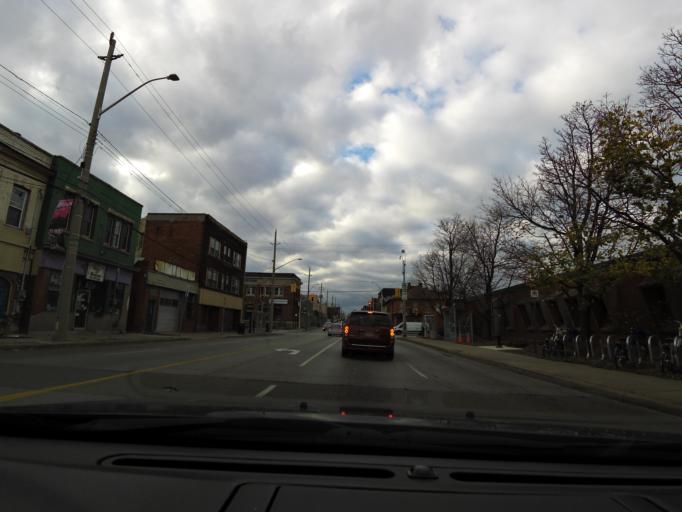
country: CA
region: Ontario
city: Hamilton
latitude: 43.2590
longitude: -79.8452
